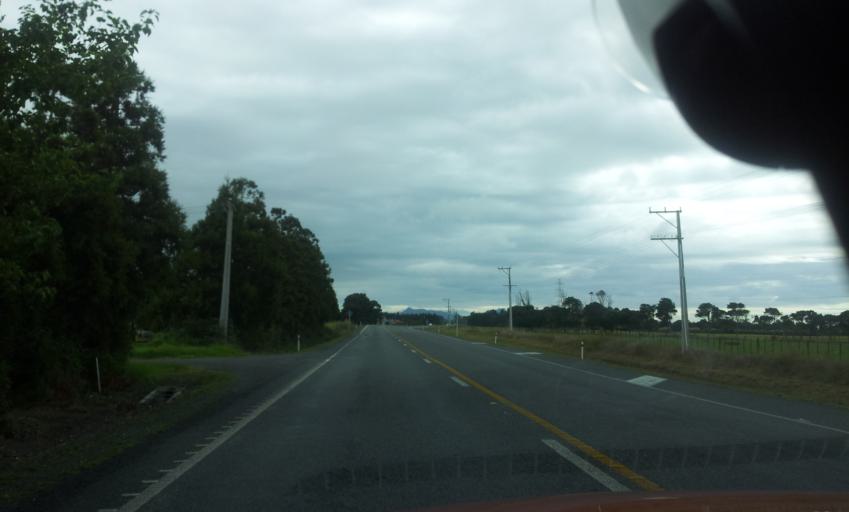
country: NZ
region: Northland
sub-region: Whangarei
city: Ruakaka
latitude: -35.9954
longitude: 174.4197
